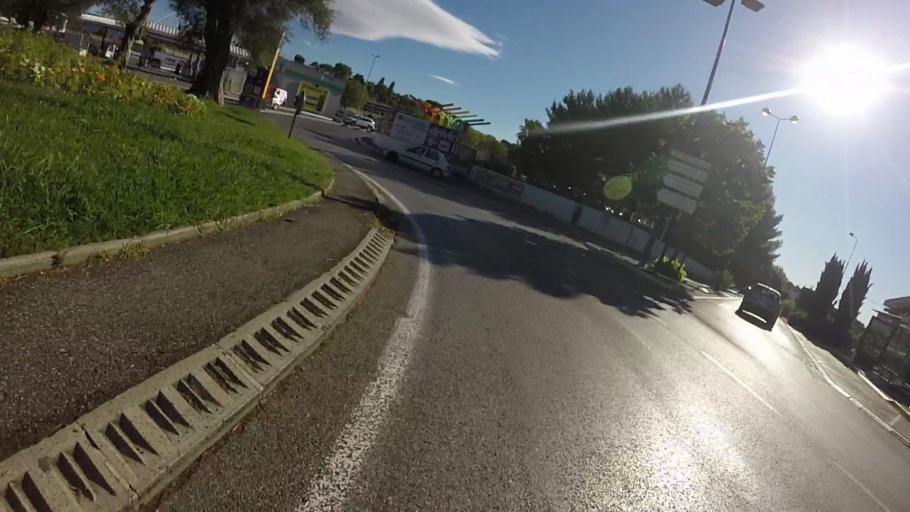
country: FR
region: Provence-Alpes-Cote d'Azur
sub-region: Departement des Alpes-Maritimes
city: Biot
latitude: 43.6024
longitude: 7.0854
